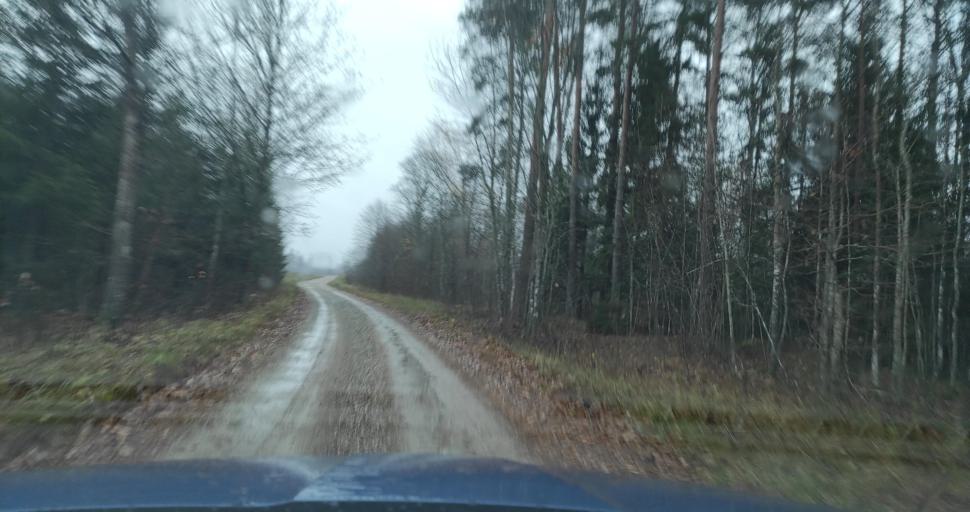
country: LV
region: Alsunga
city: Alsunga
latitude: 56.8904
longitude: 21.5874
